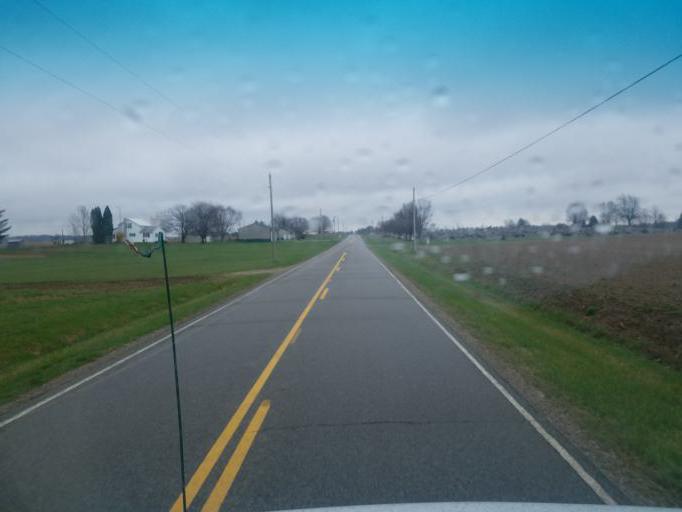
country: US
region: Ohio
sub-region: Crawford County
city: Bucyrus
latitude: 40.9068
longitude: -83.0112
